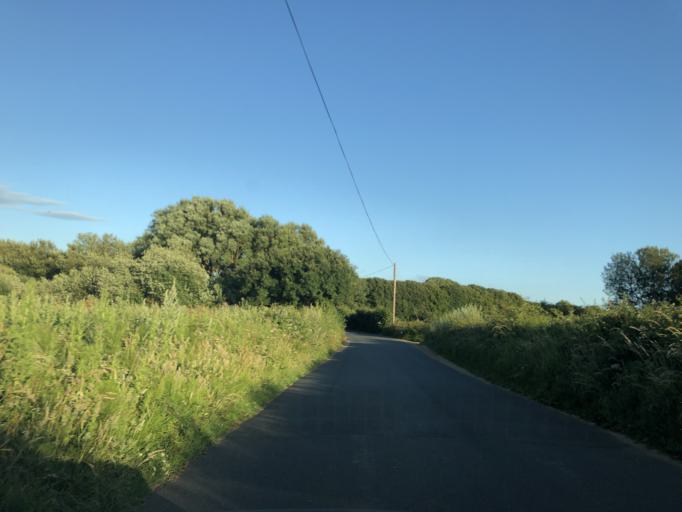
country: GB
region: England
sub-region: Isle of Wight
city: Chale
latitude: 50.6323
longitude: -1.3254
